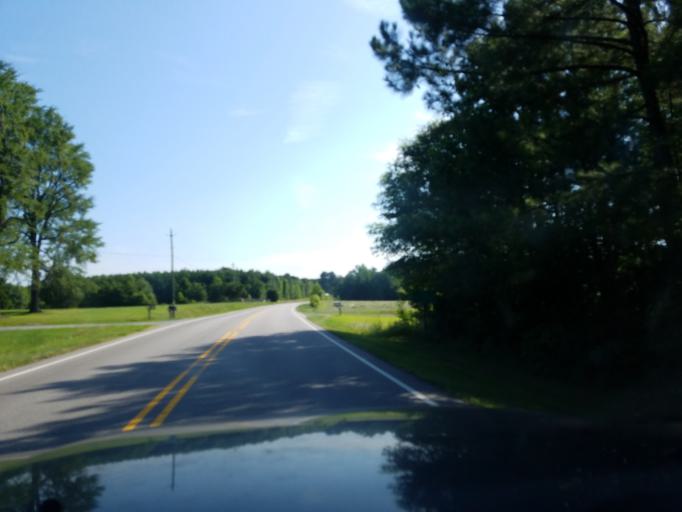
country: US
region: North Carolina
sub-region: Granville County
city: Butner
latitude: 36.1785
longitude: -78.7521
